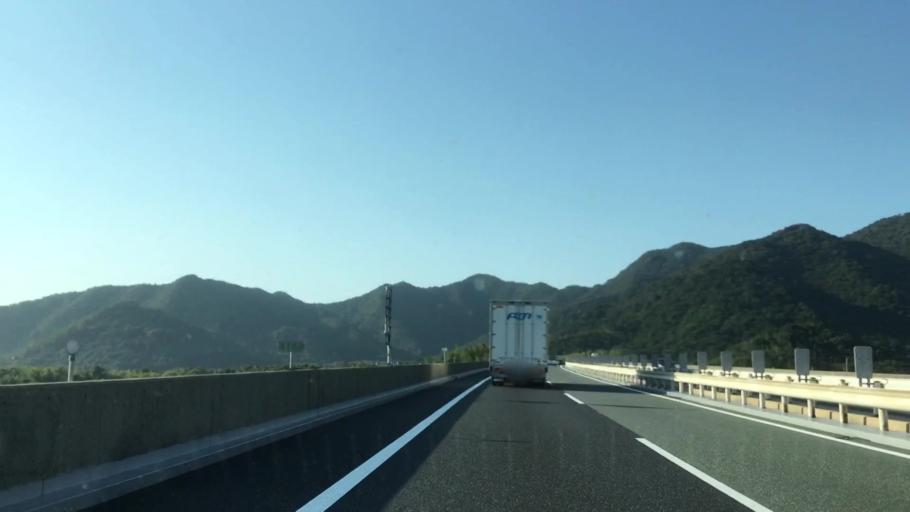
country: JP
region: Yamaguchi
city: Ogori-shimogo
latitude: 34.0938
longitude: 131.4553
